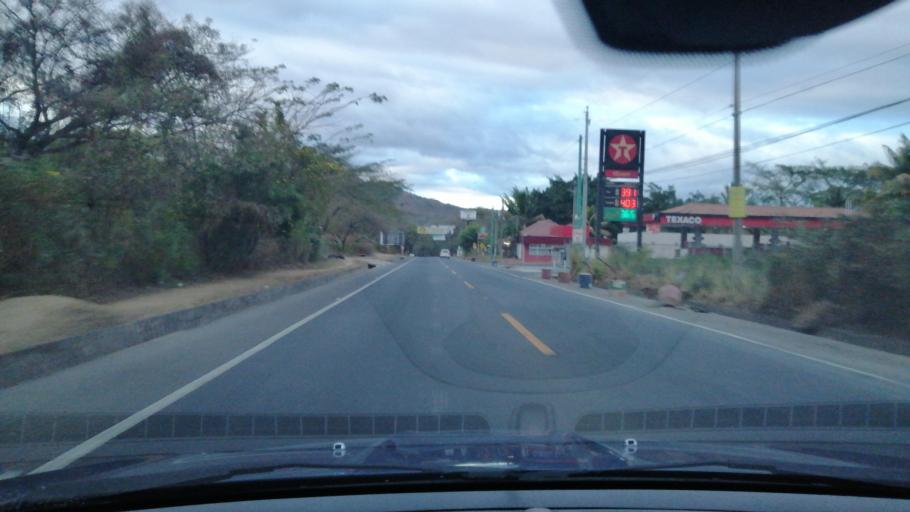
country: SV
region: Santa Ana
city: Santa Ana
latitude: 14.0037
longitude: -89.5418
